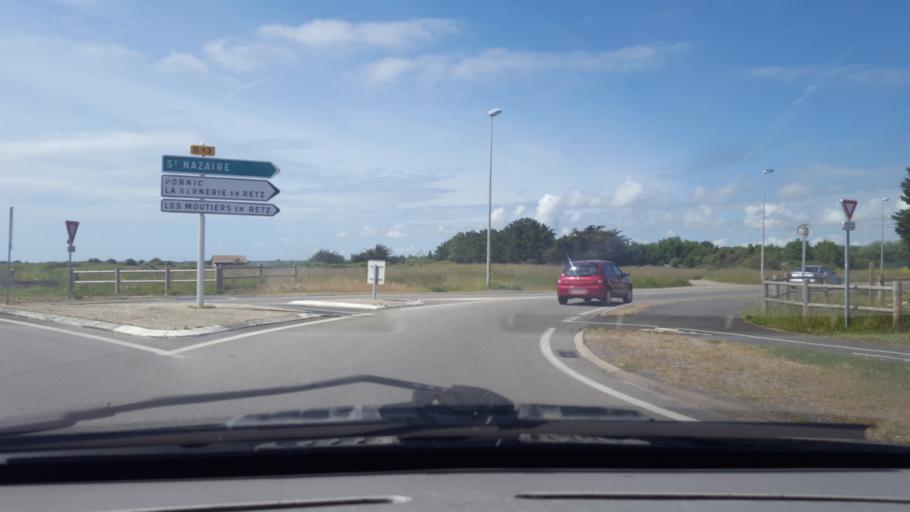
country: FR
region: Pays de la Loire
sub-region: Departement de la Loire-Atlantique
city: Bourgneuf-en-Retz
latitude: 47.0403
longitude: -1.9572
